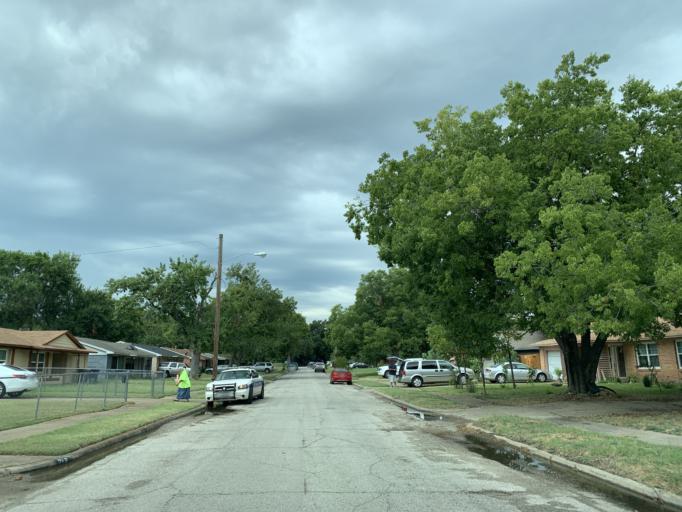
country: US
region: Texas
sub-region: Dallas County
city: DeSoto
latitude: 32.6660
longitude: -96.8257
